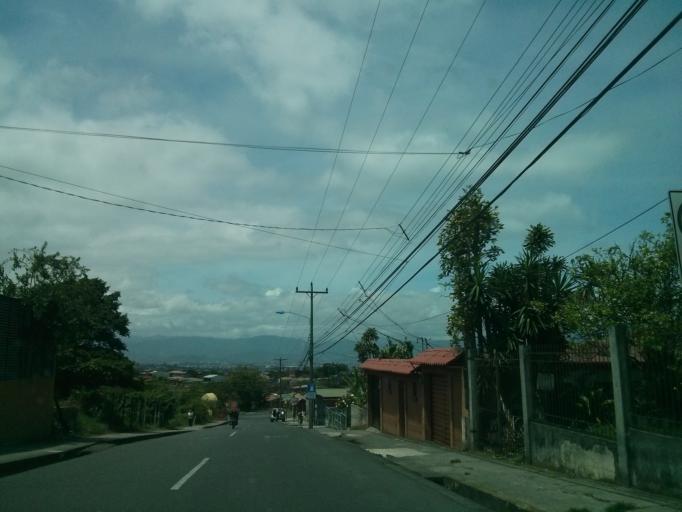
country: CR
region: Heredia
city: Angeles
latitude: 10.0157
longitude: -84.0572
